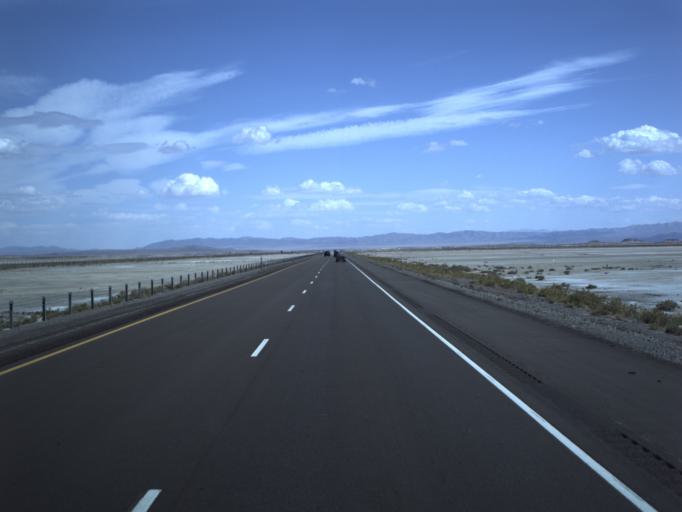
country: US
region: Utah
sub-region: Tooele County
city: Wendover
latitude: 40.7276
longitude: -113.3401
